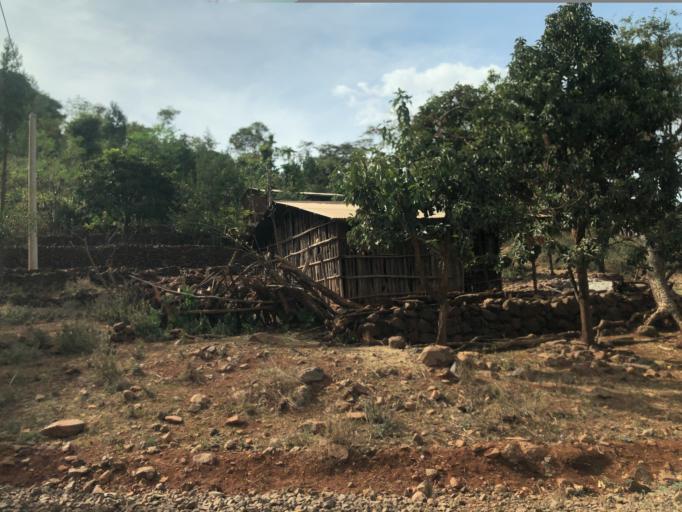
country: ET
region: Southern Nations, Nationalities, and People's Region
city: Konso
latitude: 5.3298
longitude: 37.4042
